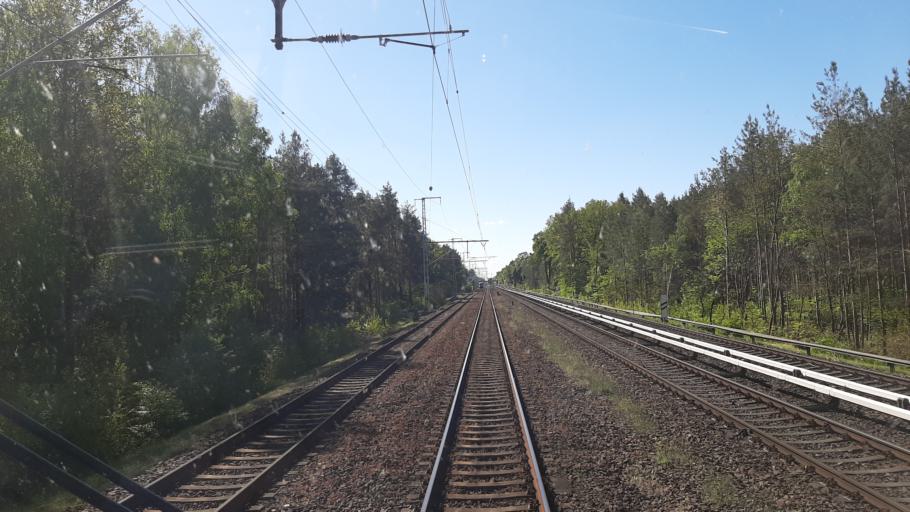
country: DE
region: Brandenburg
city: Birkenwerder
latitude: 52.7248
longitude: 13.2721
